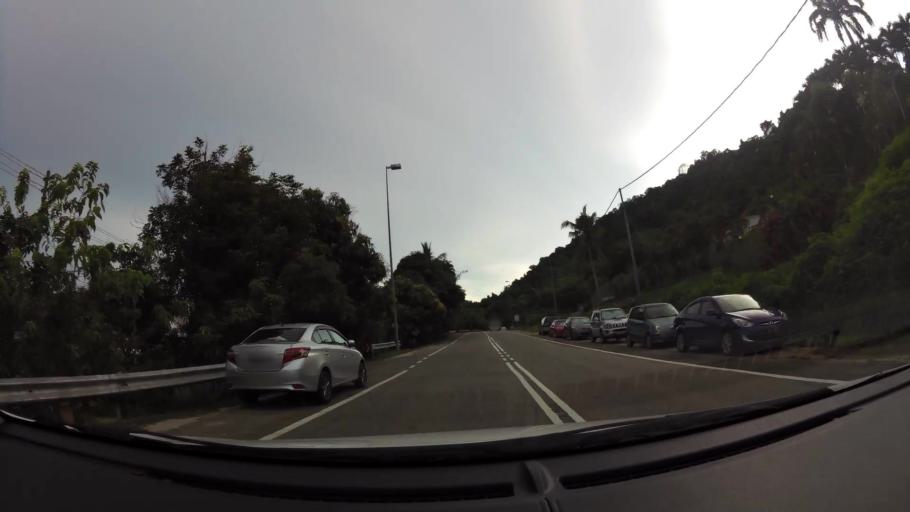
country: BN
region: Brunei and Muara
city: Bandar Seri Begawan
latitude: 4.9231
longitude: 115.0112
